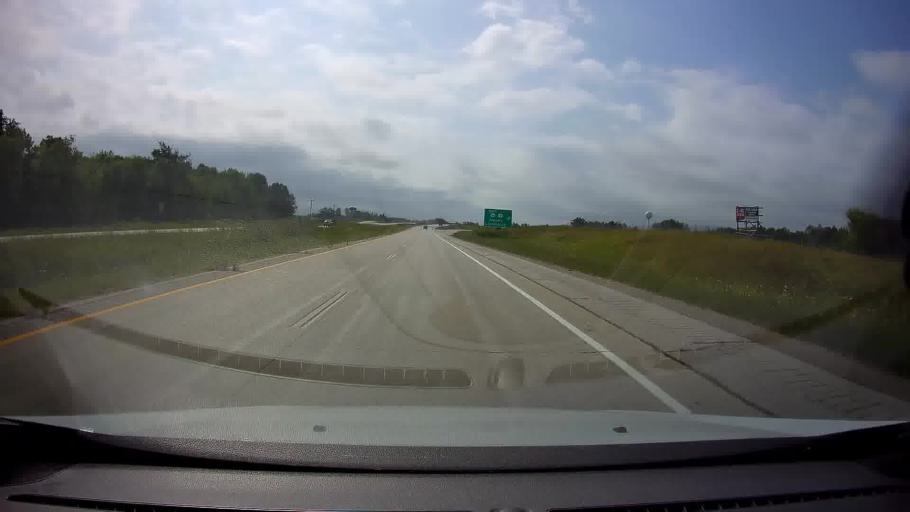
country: US
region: Wisconsin
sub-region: Brown County
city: Bellevue
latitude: 44.5456
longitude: -87.8812
